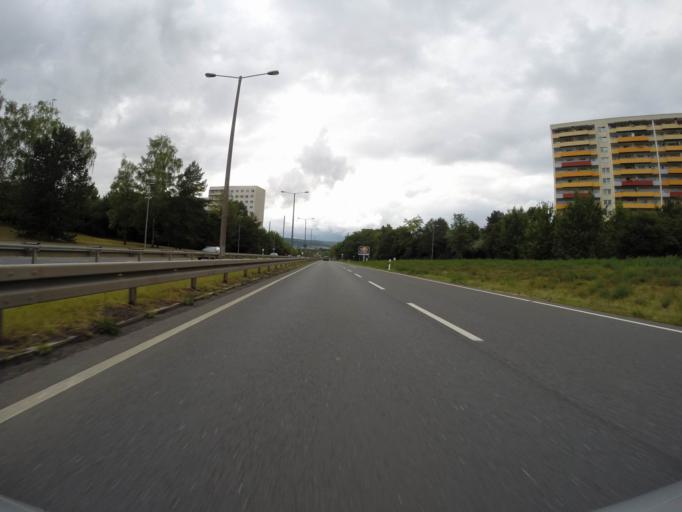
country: DE
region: Thuringia
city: Sulza
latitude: 50.8881
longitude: 11.6093
